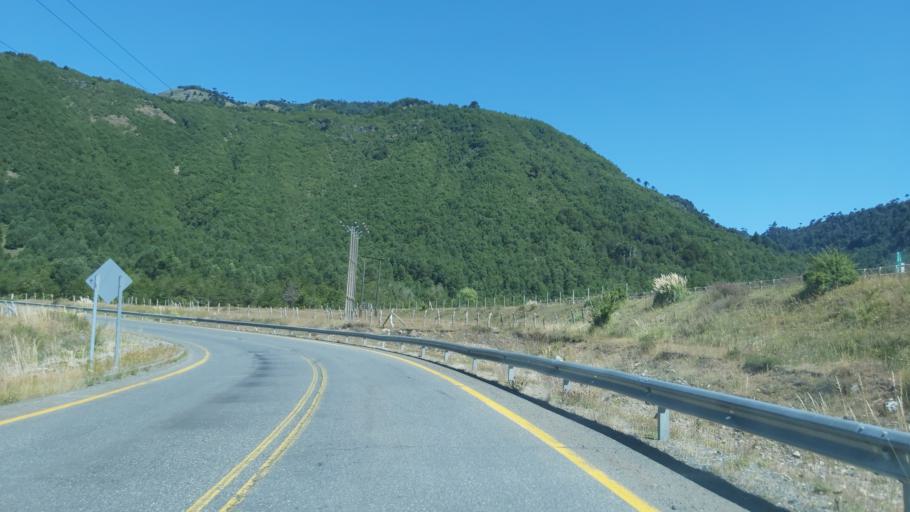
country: CL
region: Araucania
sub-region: Provincia de Cautin
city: Vilcun
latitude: -38.5667
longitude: -71.4926
